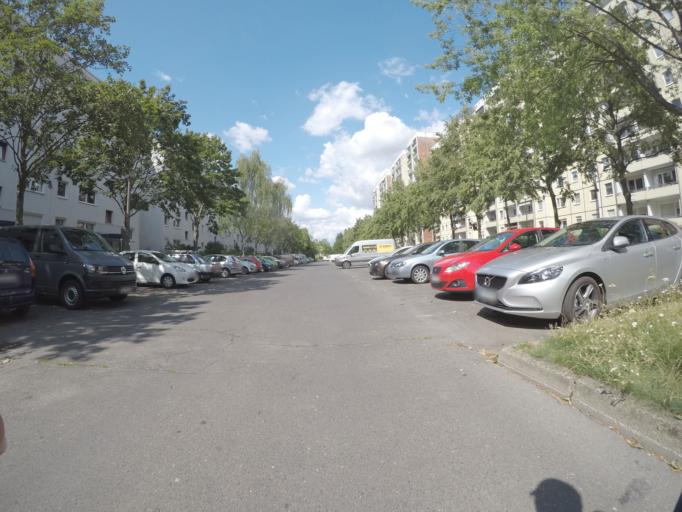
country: DE
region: Berlin
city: Kaulsdorf
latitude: 52.5182
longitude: 13.5828
